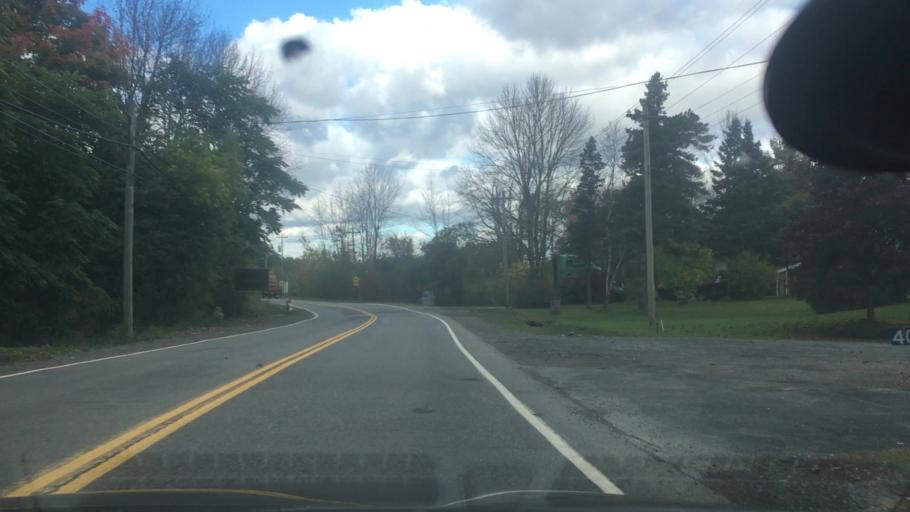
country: CA
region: Nova Scotia
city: Windsor
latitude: 44.9755
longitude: -64.1187
